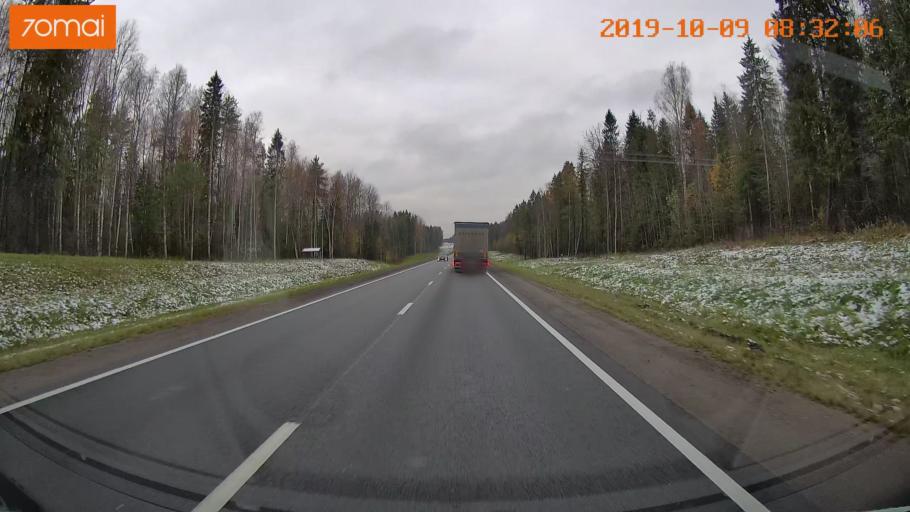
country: RU
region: Vologda
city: Gryazovets
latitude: 58.8622
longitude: 40.1986
